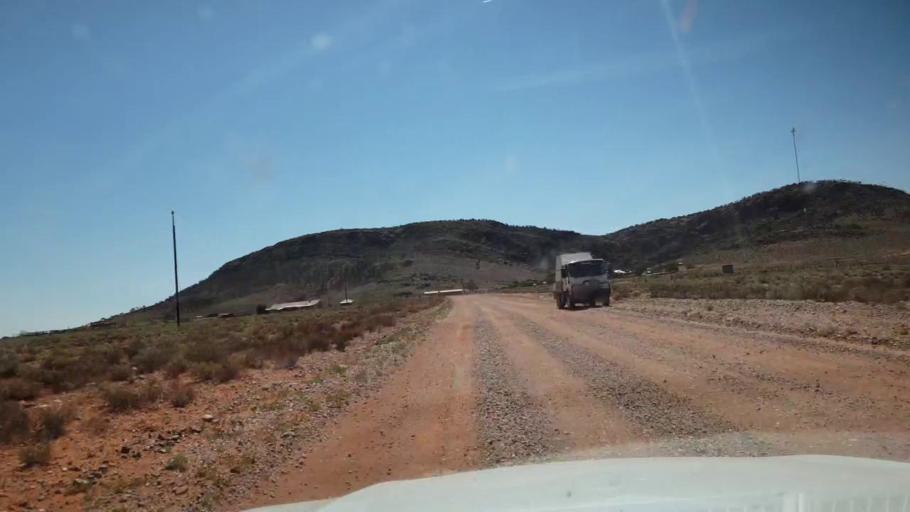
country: AU
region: South Australia
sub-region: Whyalla
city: Whyalla
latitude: -32.6885
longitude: 137.1272
